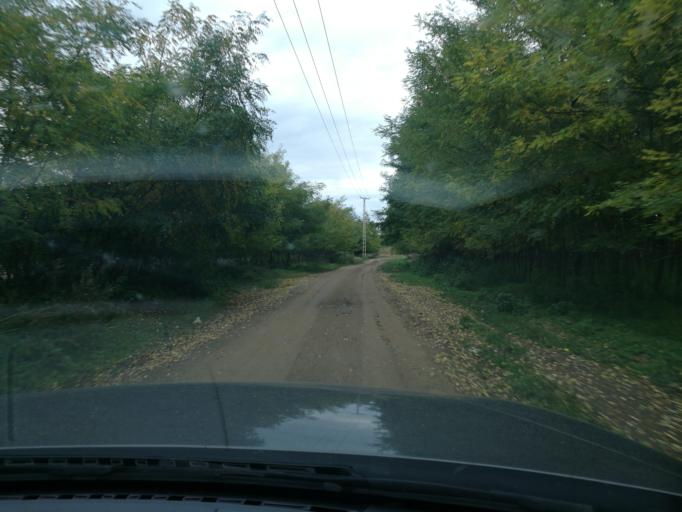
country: HU
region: Szabolcs-Szatmar-Bereg
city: Nyirpazony
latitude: 47.9973
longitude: 21.7956
